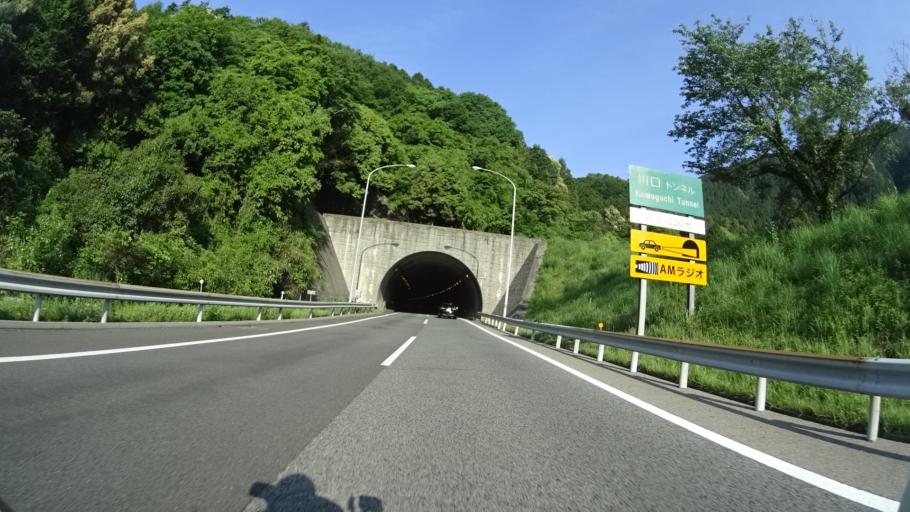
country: JP
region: Ehime
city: Saijo
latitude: 33.9092
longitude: 133.2520
